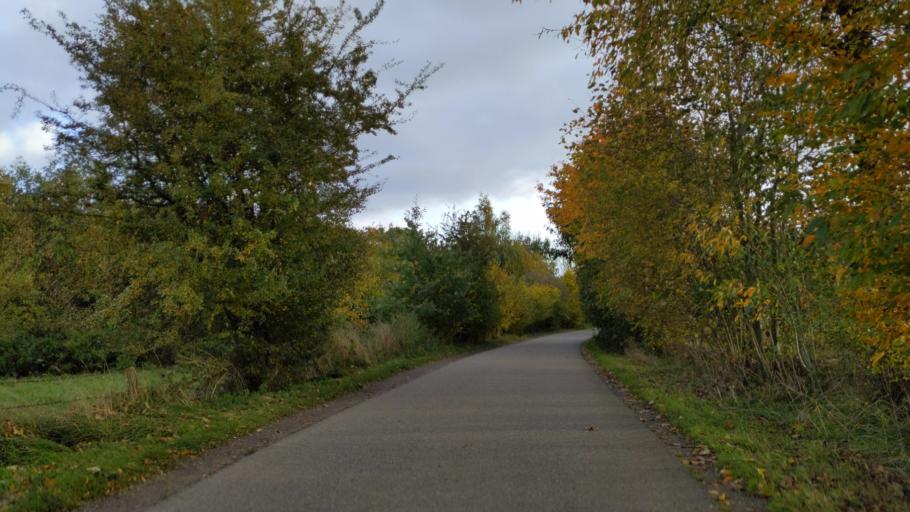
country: DE
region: Schleswig-Holstein
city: Susel
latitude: 54.1142
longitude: 10.7054
